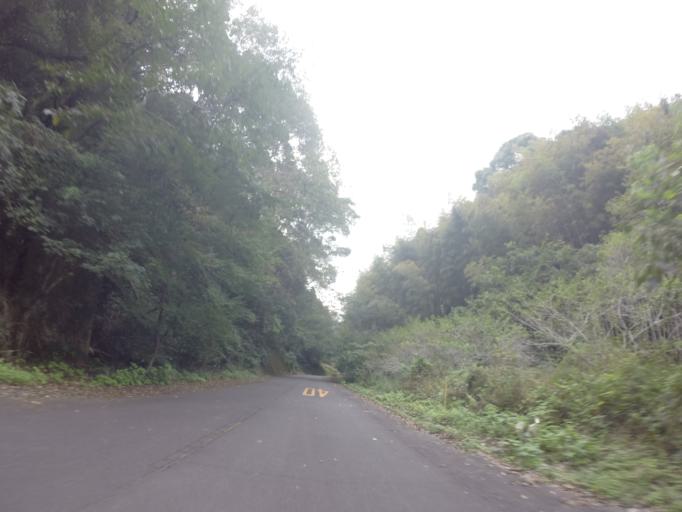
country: JP
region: Shizuoka
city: Fujieda
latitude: 34.9198
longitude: 138.2274
